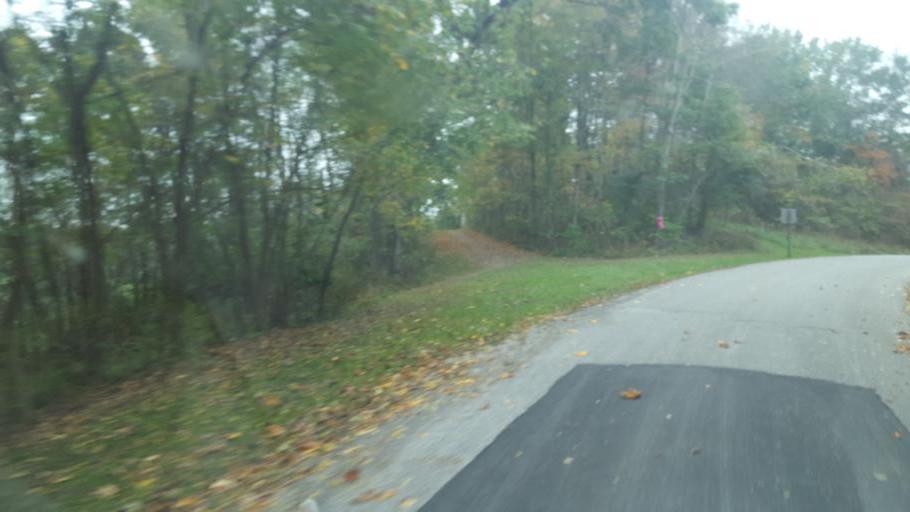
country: US
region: Ohio
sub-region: Harrison County
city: Cadiz
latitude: 40.3744
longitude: -81.0456
